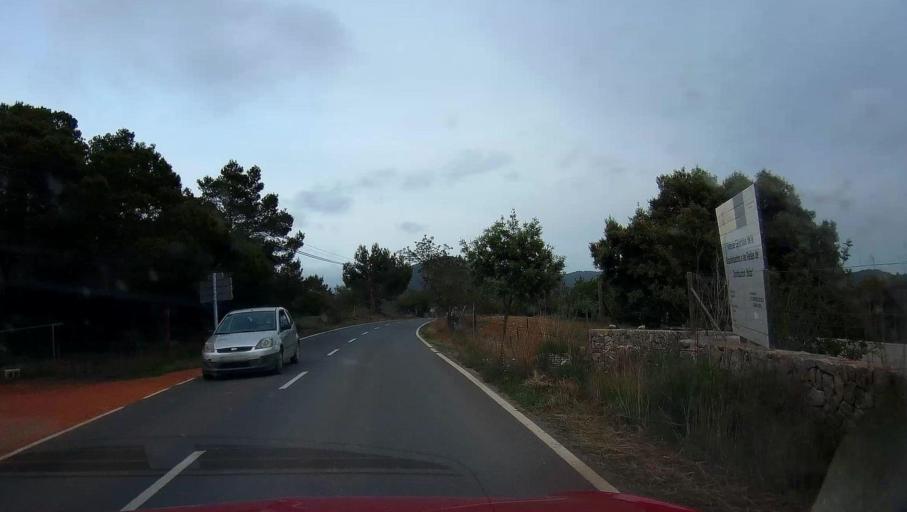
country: ES
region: Balearic Islands
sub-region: Illes Balears
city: Sant Joan de Labritja
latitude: 39.0492
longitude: 1.4285
